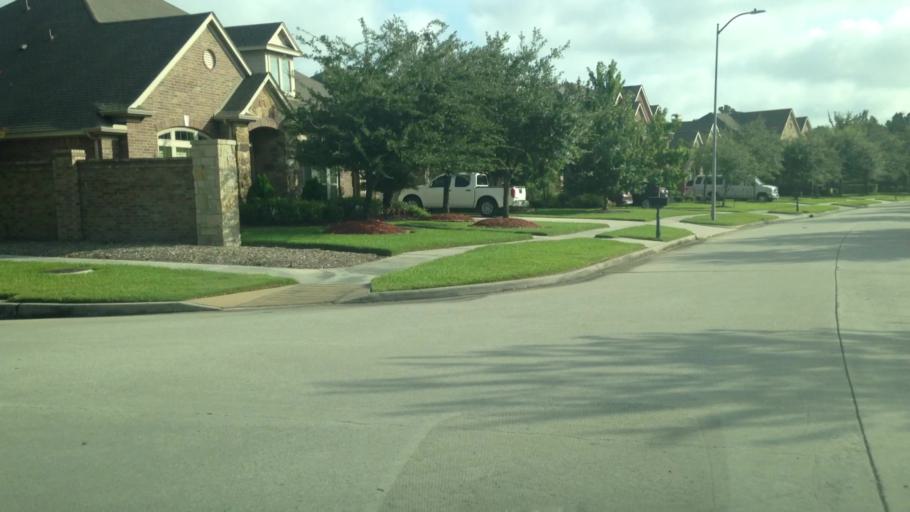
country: US
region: Texas
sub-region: Harris County
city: Sheldon
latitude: 29.9225
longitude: -95.1706
